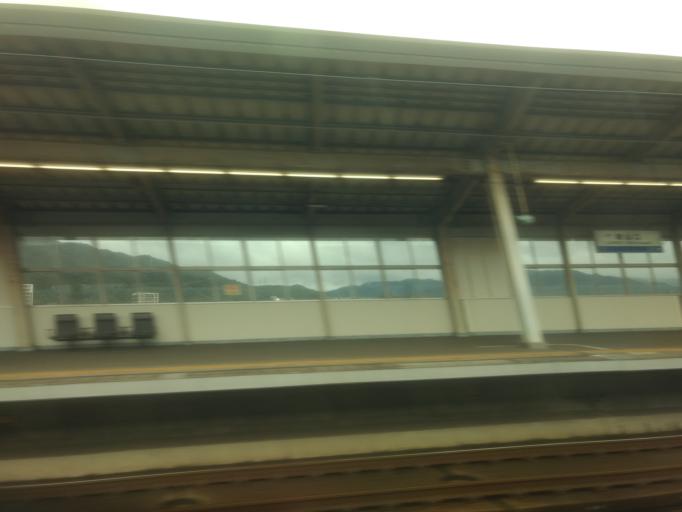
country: JP
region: Yamaguchi
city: Ogori-shimogo
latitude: 34.0936
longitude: 131.3978
